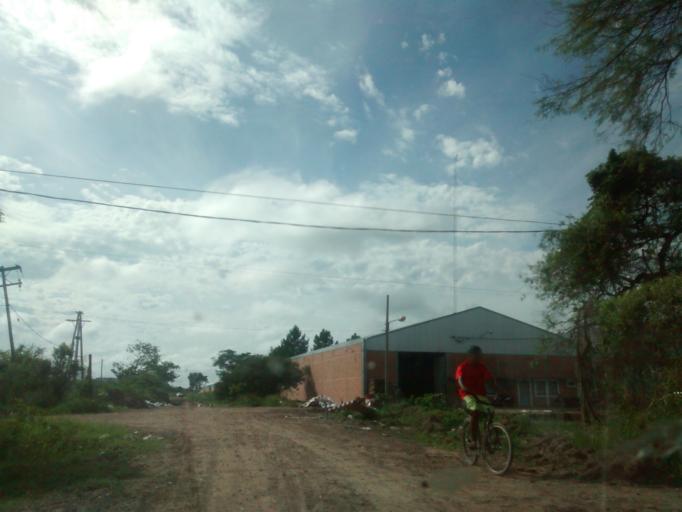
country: AR
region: Chaco
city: Fontana
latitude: -27.4060
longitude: -58.9800
